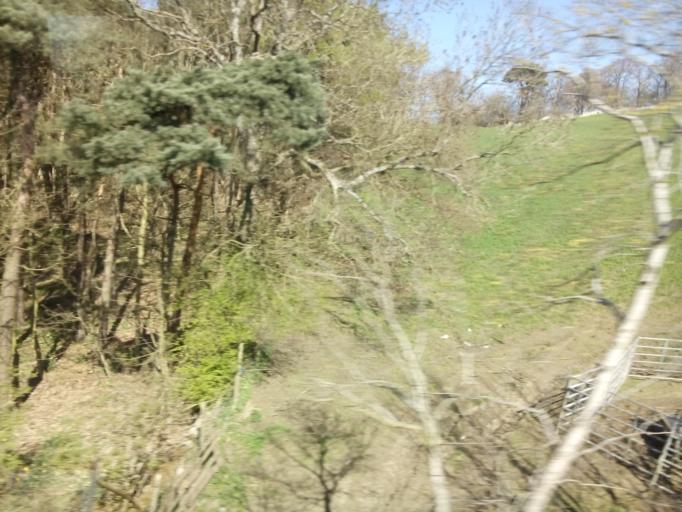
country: GB
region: Scotland
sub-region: Fife
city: Crossgates
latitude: 56.0474
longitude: -3.3446
